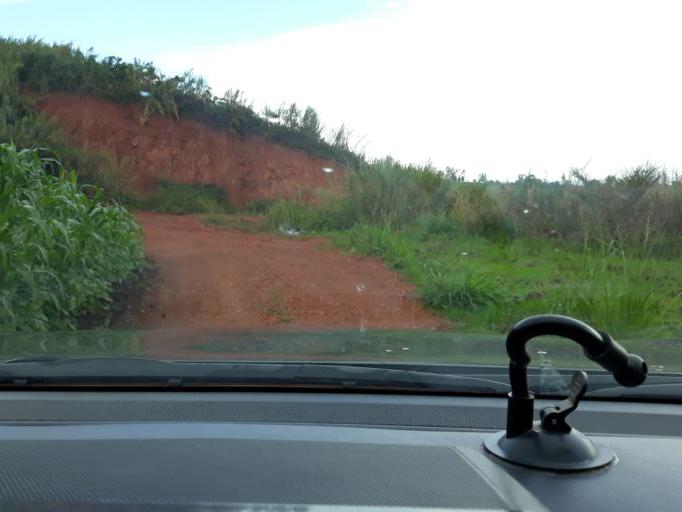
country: CD
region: Eastern Province
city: Bunia
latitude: 1.6975
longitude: 30.2823
